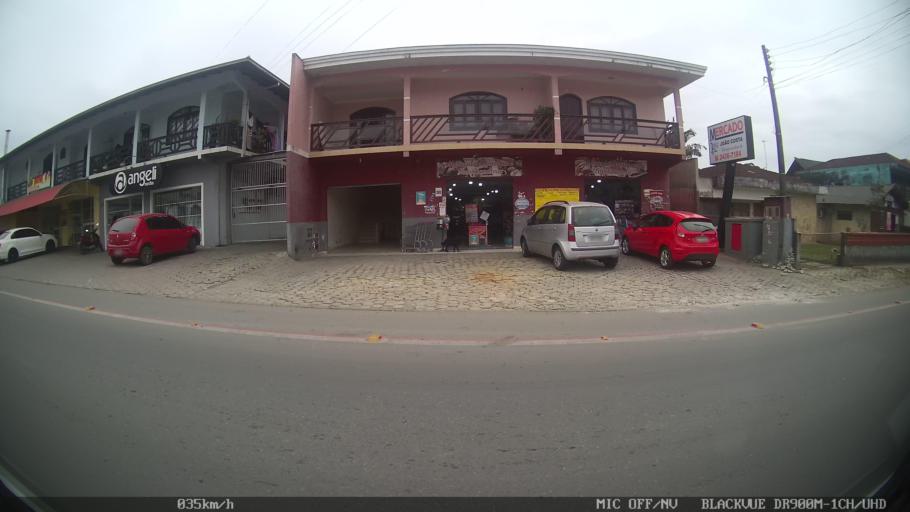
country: BR
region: Santa Catarina
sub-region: Joinville
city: Joinville
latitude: -26.3501
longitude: -48.8186
